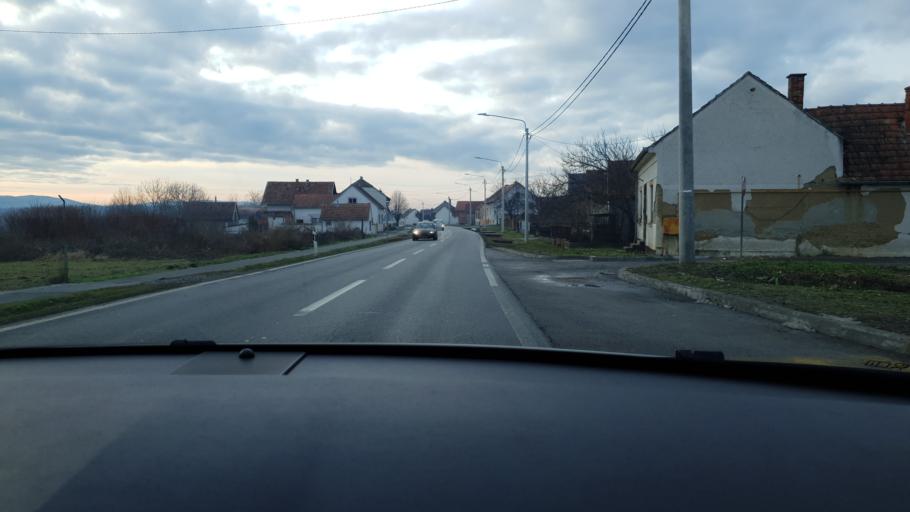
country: HR
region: Pozesko-Slavonska
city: Jaksic
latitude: 45.3576
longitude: 17.7364
